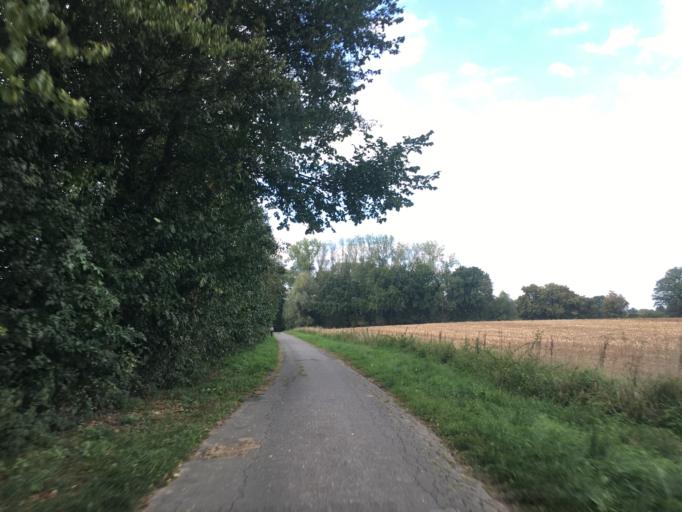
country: DE
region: North Rhine-Westphalia
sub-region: Regierungsbezirk Munster
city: Altenberge
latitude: 51.9822
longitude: 7.5199
